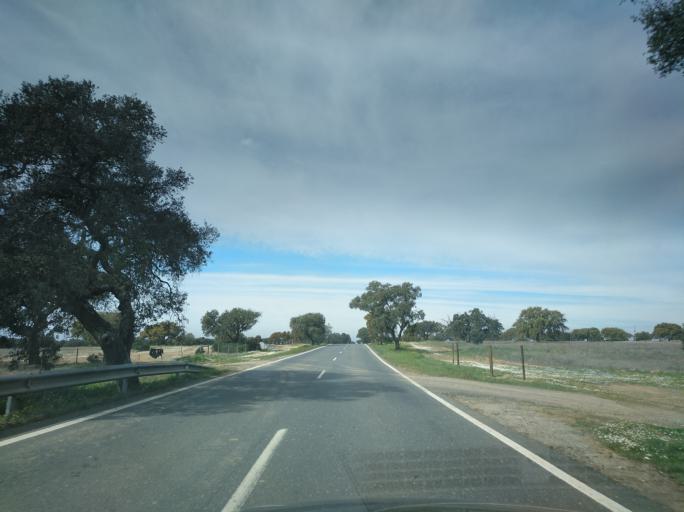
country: PT
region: Beja
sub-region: Mertola
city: Mertola
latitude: 37.7534
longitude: -7.8070
